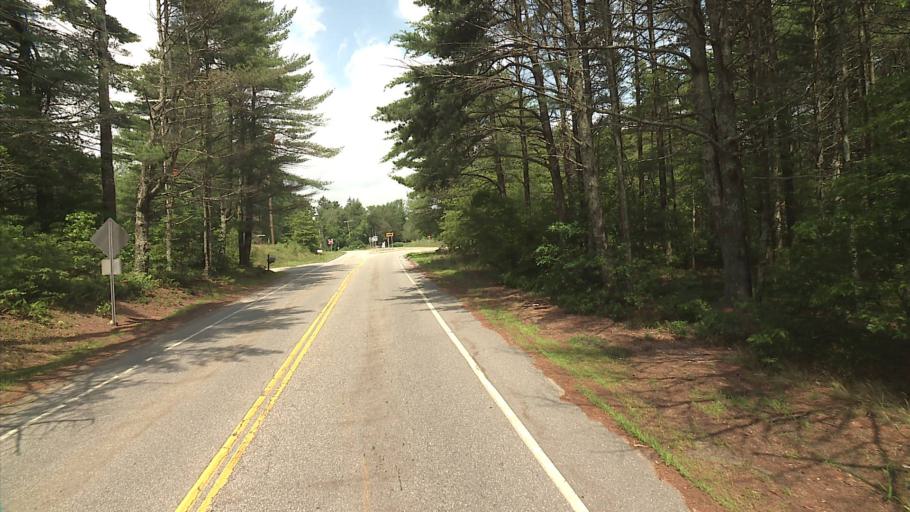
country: US
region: Rhode Island
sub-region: Washington County
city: Hopkinton
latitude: 41.5727
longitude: -71.8332
